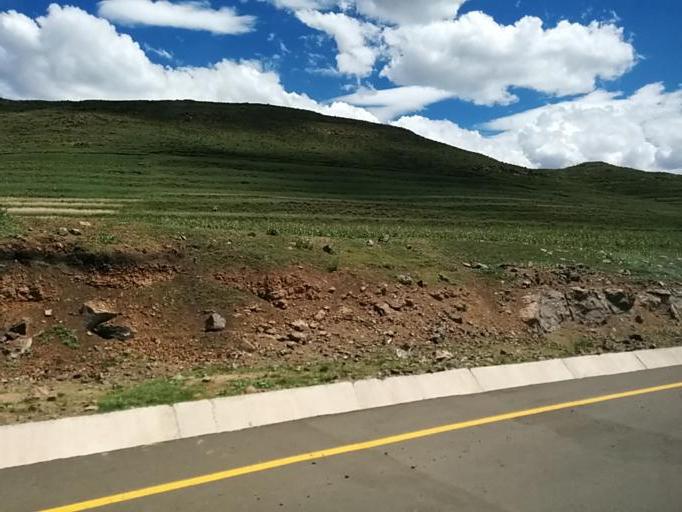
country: LS
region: Maseru
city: Nako
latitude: -29.9593
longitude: 28.1538
